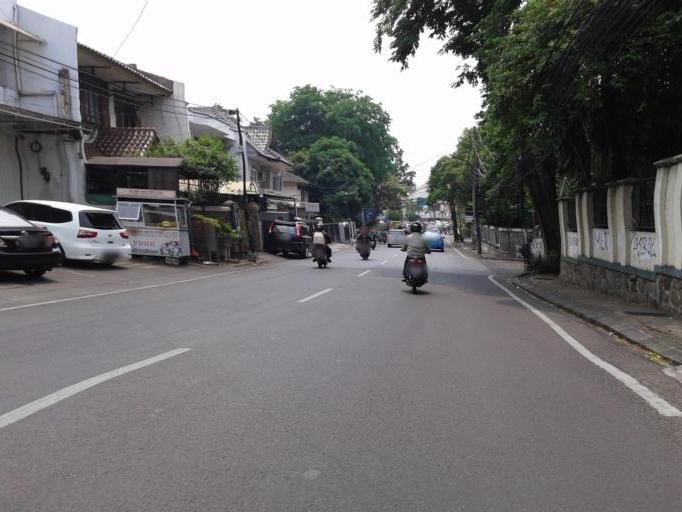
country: ID
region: Banten
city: South Tangerang
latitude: -6.2724
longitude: 106.7522
